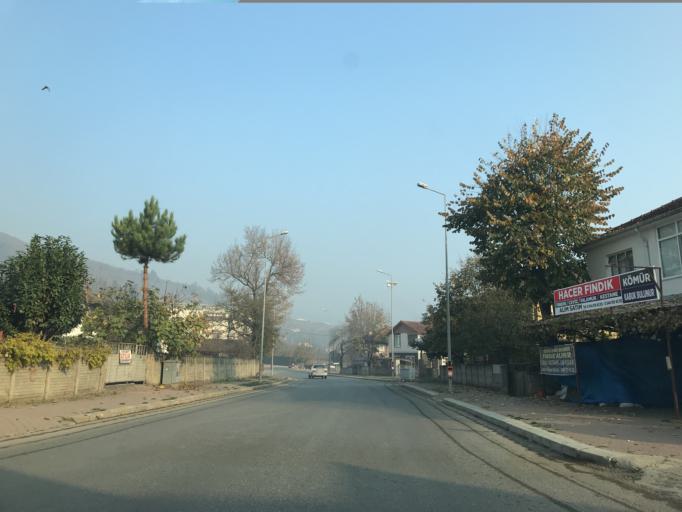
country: TR
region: Duzce
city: Cumayeri
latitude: 40.8829
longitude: 30.9514
